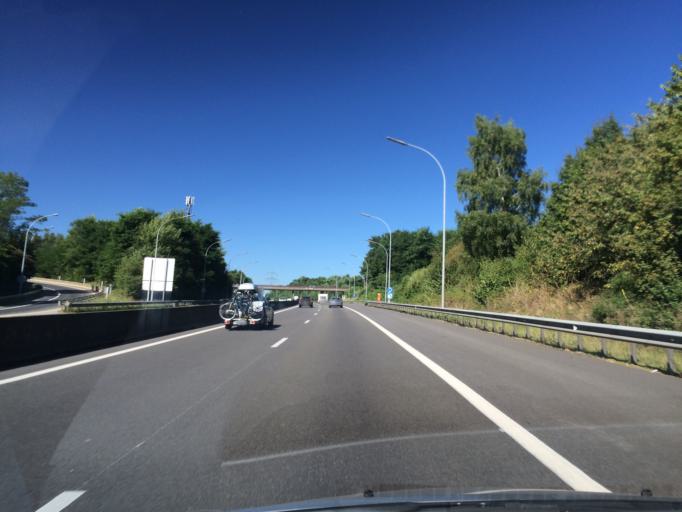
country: LU
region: Luxembourg
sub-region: Canton de Luxembourg
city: Strassen
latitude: 49.6297
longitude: 6.0683
